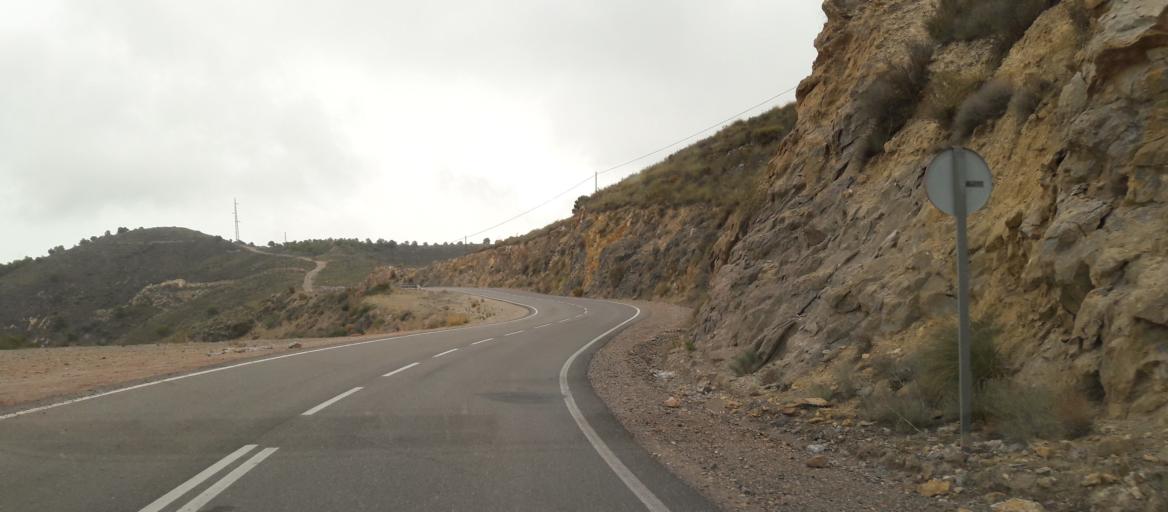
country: ES
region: Andalusia
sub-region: Provincia de Almeria
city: Enix
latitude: 36.8742
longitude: -2.6213
